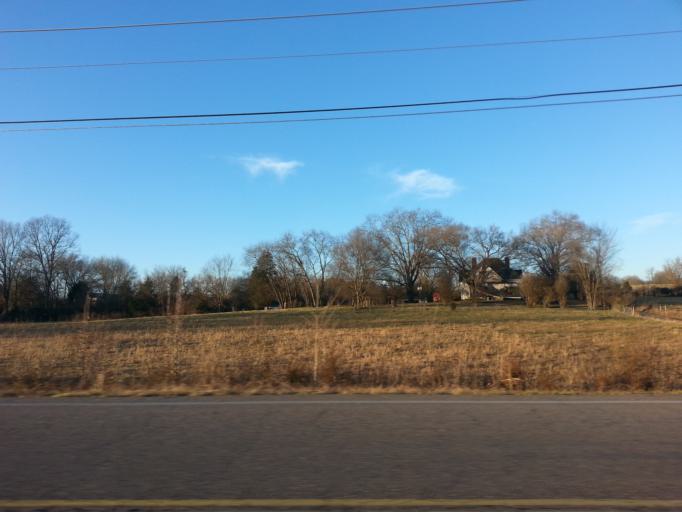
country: US
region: Tennessee
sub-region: Knox County
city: Knoxville
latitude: 35.9804
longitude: -83.8236
